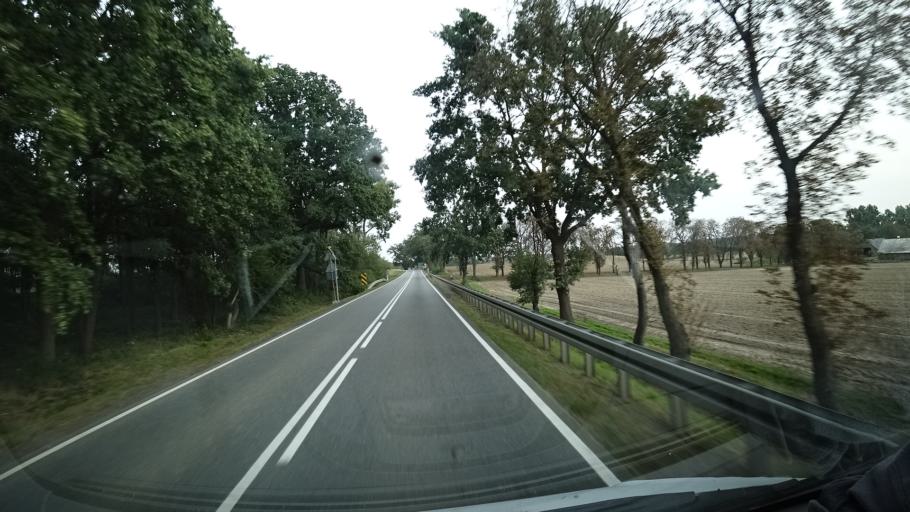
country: PL
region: Silesian Voivodeship
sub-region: Powiat gliwicki
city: Rudziniec
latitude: 50.3873
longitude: 18.4010
